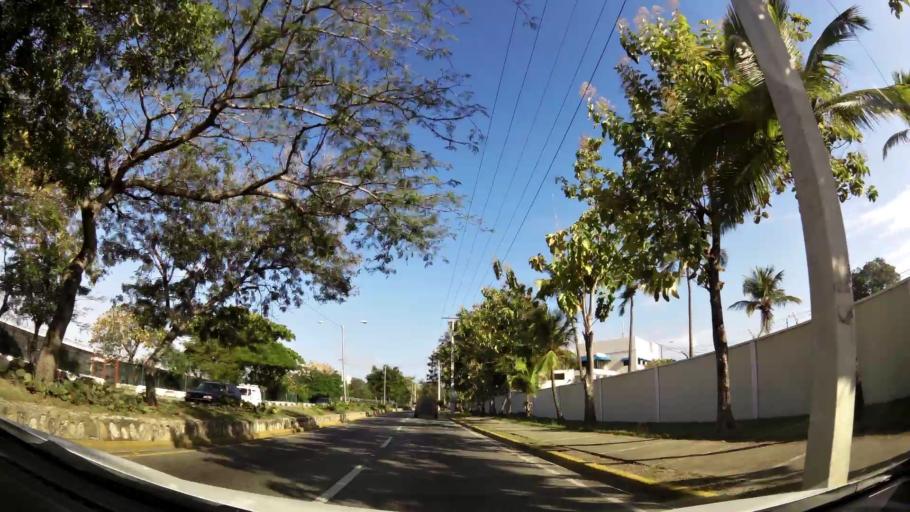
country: DO
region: Nacional
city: Ciudad Nueva
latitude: 18.4705
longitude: -69.8749
